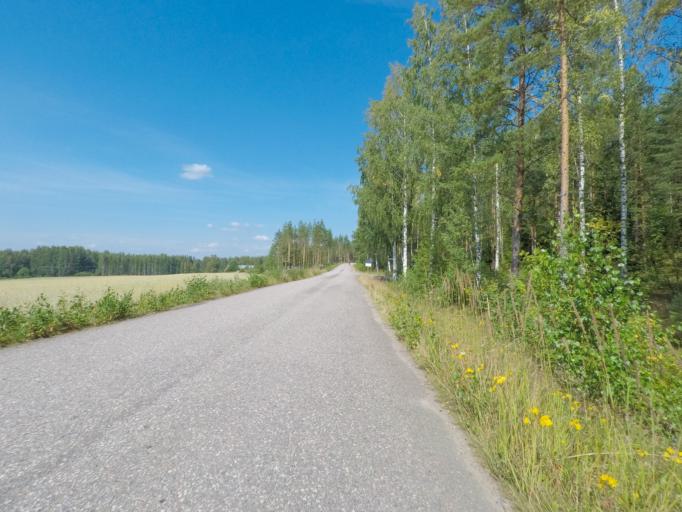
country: FI
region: Southern Savonia
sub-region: Mikkeli
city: Puumala
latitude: 61.4151
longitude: 28.0920
